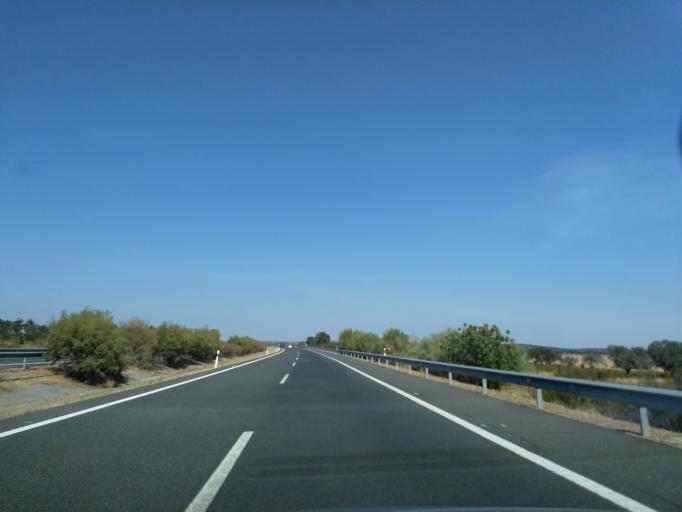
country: ES
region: Extremadura
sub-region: Provincia de Caceres
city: Casas de Don Antonio
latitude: 39.2104
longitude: -6.2858
